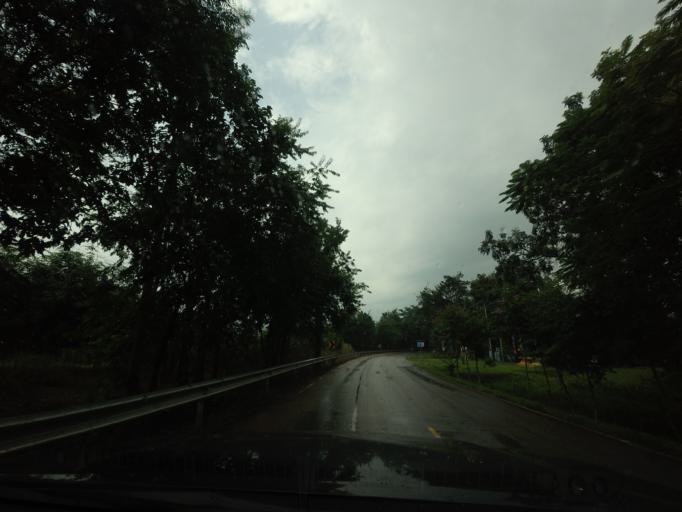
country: TH
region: Nong Khai
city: Sangkhom
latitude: 18.0921
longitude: 102.2456
